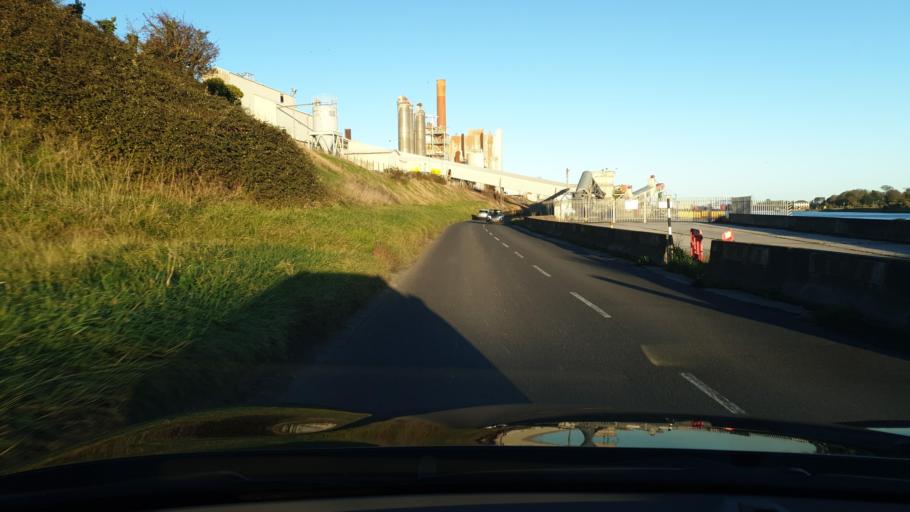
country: IE
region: Leinster
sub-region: Lu
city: Drogheda
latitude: 53.7203
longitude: -6.3220
